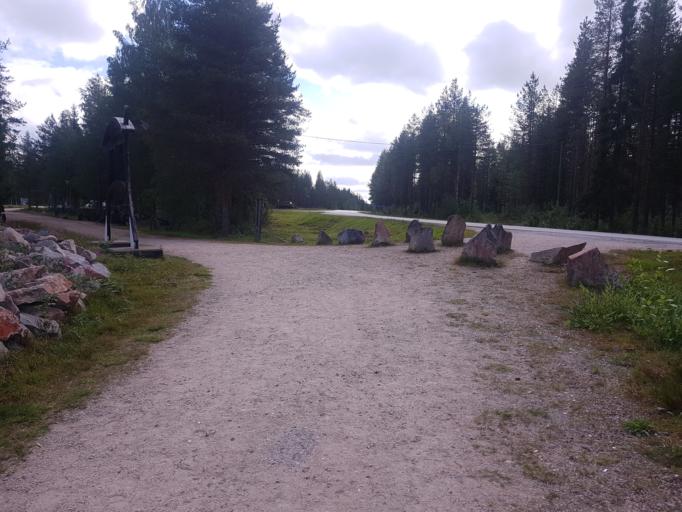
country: FI
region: Kainuu
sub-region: Kehys-Kainuu
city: Suomussalmi
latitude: 64.8487
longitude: 29.3250
